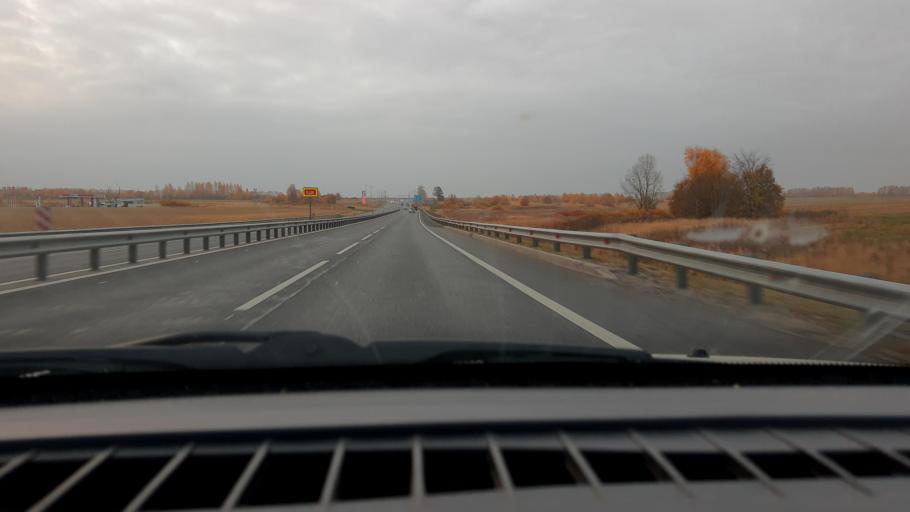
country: RU
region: Nizjnij Novgorod
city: Burevestnik
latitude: 56.1302
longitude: 43.9148
